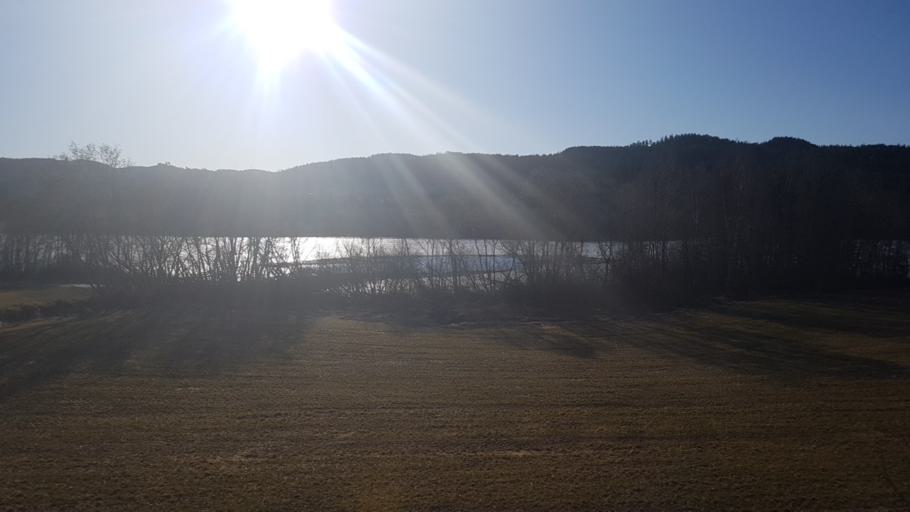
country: NO
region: Nord-Trondelag
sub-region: Levanger
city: Skogn
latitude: 63.6364
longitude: 11.0720
